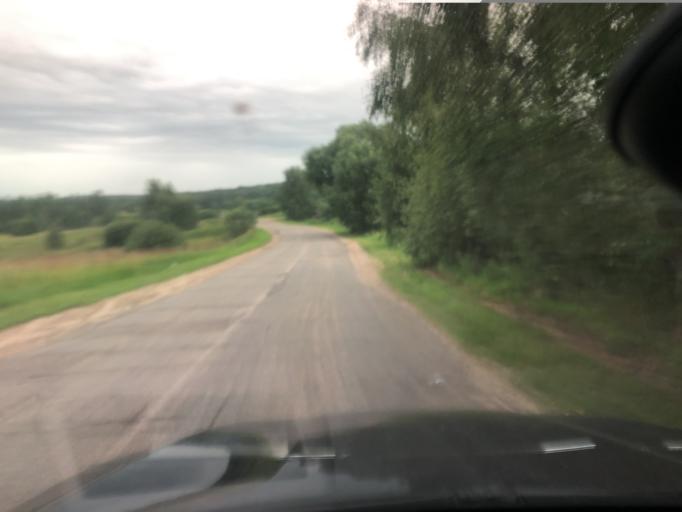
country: RU
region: Jaroslavl
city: Petrovsk
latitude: 56.9873
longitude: 39.1778
